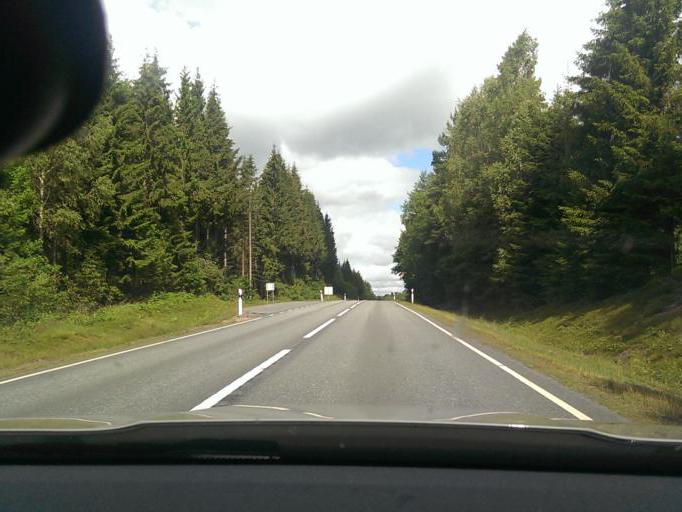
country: SE
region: Joenkoeping
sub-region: Varnamo Kommun
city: Varnamo
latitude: 57.2141
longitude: 14.0197
